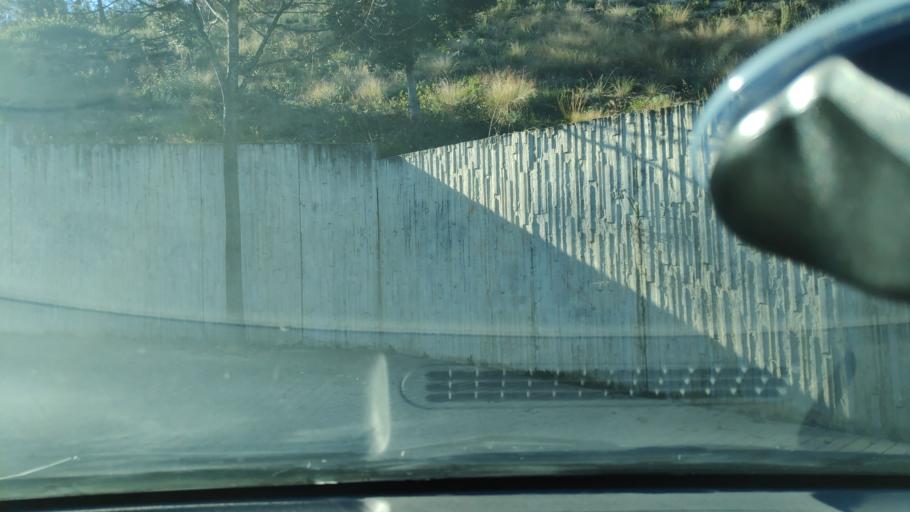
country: ES
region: Catalonia
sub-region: Provincia de Barcelona
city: Sant Quirze del Valles
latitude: 41.5299
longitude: 2.0685
